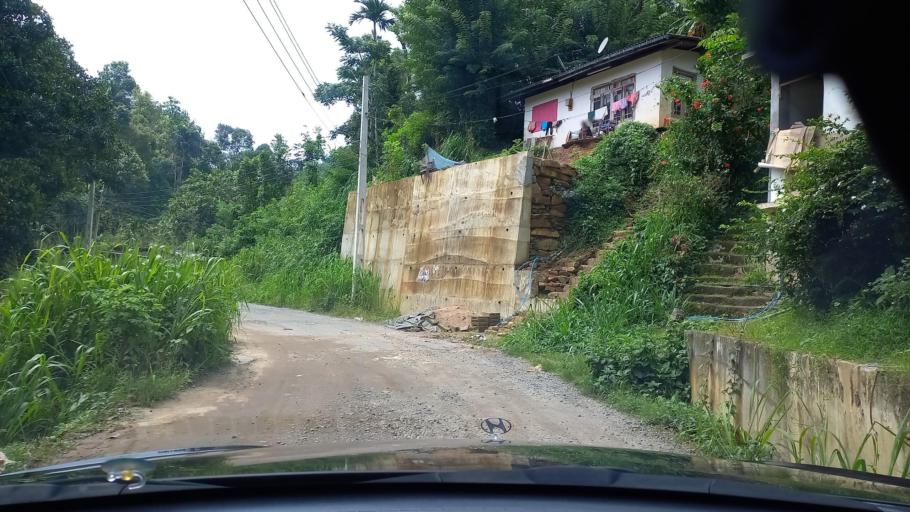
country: LK
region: Central
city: Gampola
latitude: 7.2178
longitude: 80.6142
